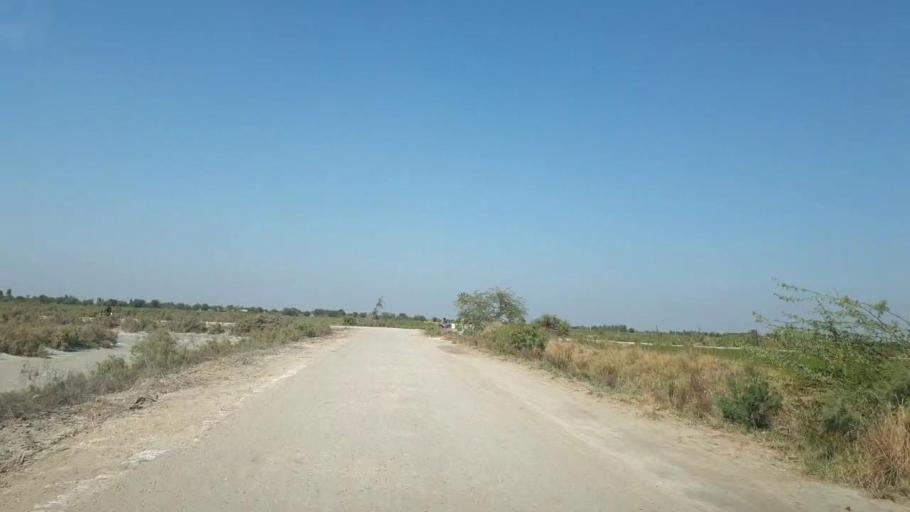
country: PK
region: Sindh
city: Mirpur Khas
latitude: 25.6672
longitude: 69.0266
